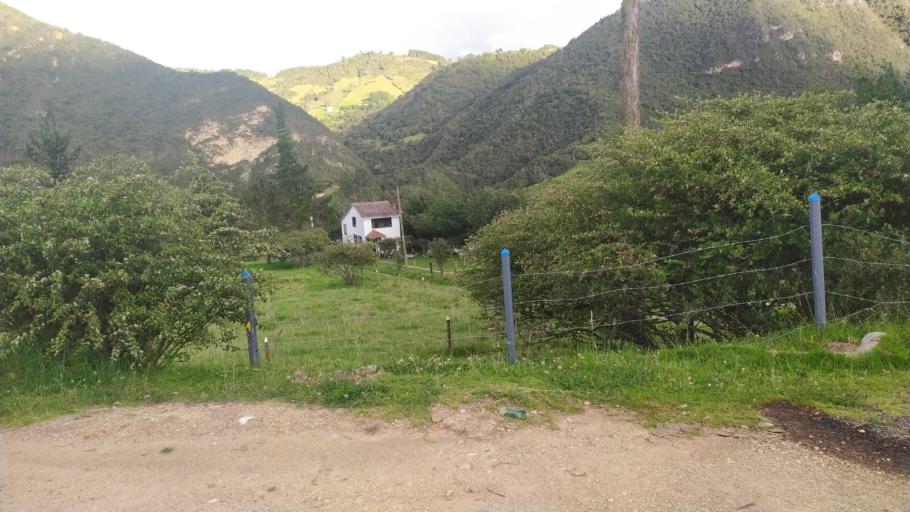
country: CO
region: Cundinamarca
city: La Calera
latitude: 4.7461
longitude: -73.9520
